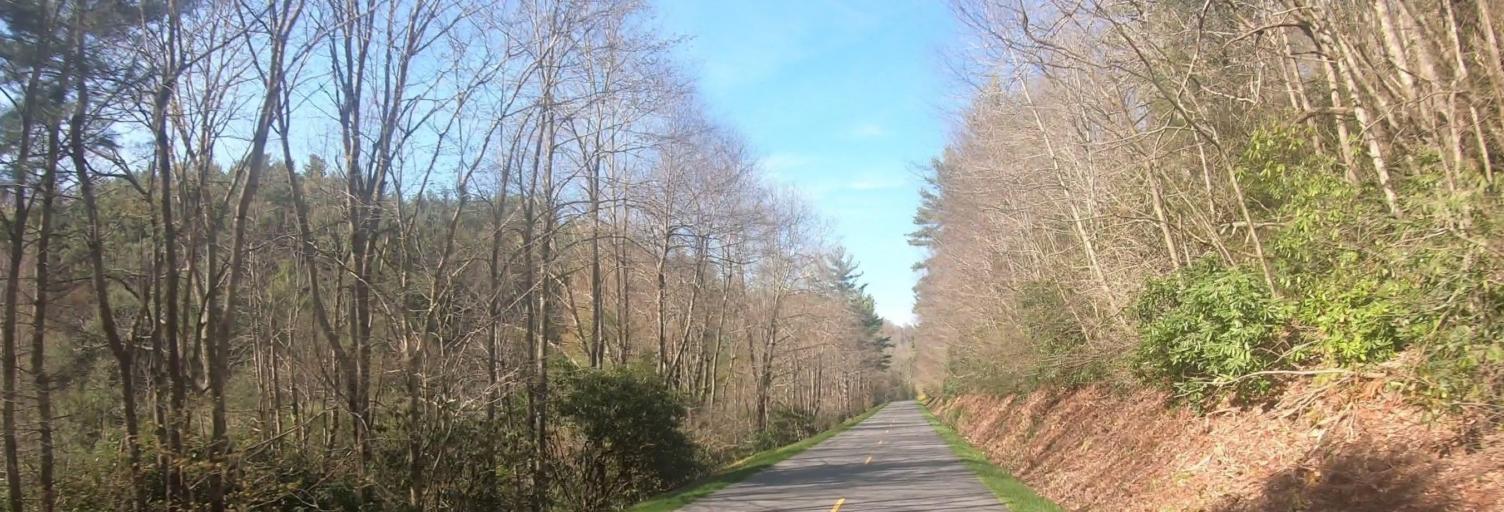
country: US
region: North Carolina
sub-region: Watauga County
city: Blowing Rock
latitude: 36.1696
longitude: -81.6157
